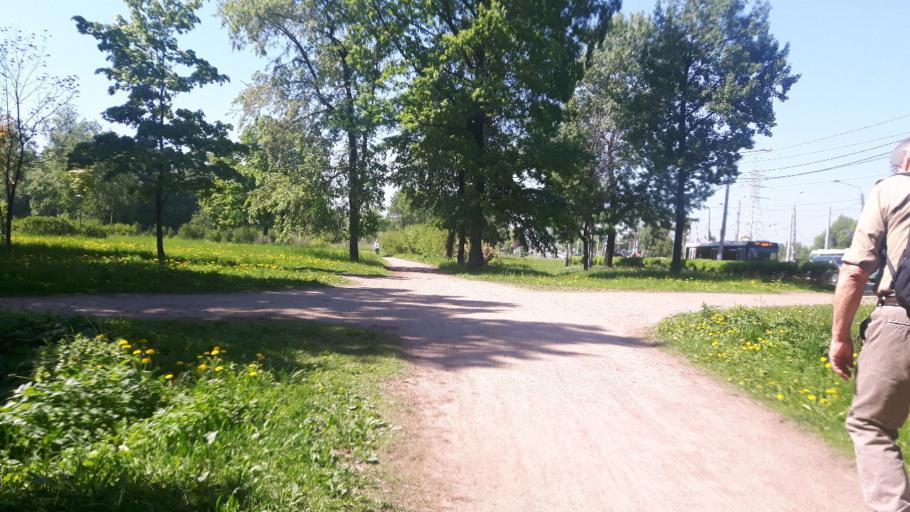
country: RU
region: St.-Petersburg
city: Sosnovaya Polyana
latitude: 59.8479
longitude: 30.1268
